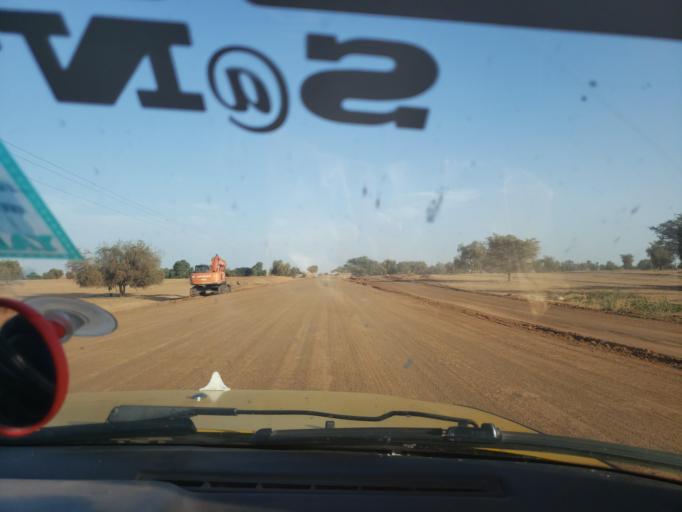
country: SN
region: Louga
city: Dara
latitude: 15.4170
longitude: -15.7148
